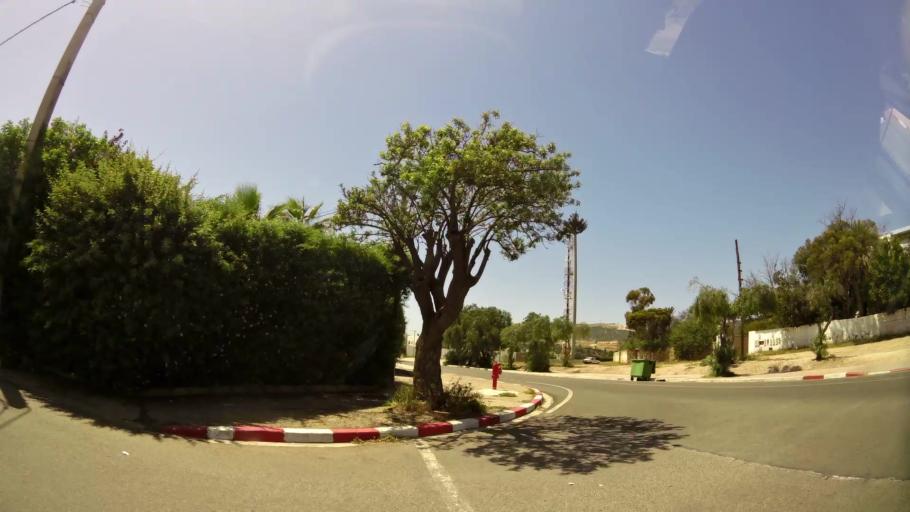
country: MA
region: Souss-Massa-Draa
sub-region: Agadir-Ida-ou-Tnan
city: Agadir
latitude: 30.4311
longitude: -9.5973
